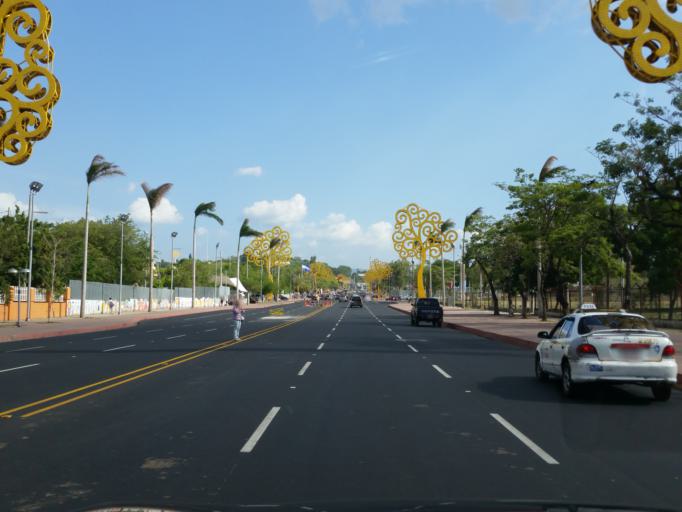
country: NI
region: Managua
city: Managua
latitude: 12.1530
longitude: -86.2740
